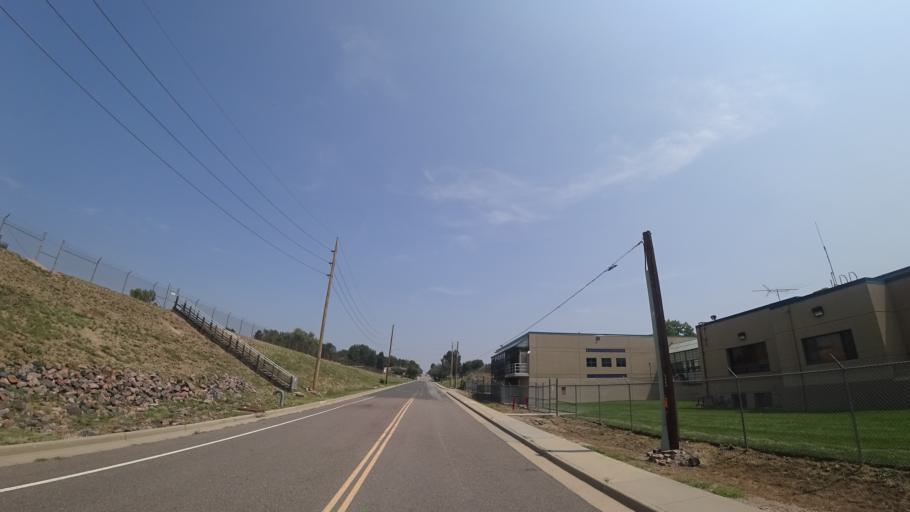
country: US
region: Colorado
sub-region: Arapahoe County
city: Littleton
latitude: 39.6296
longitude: -105.0056
